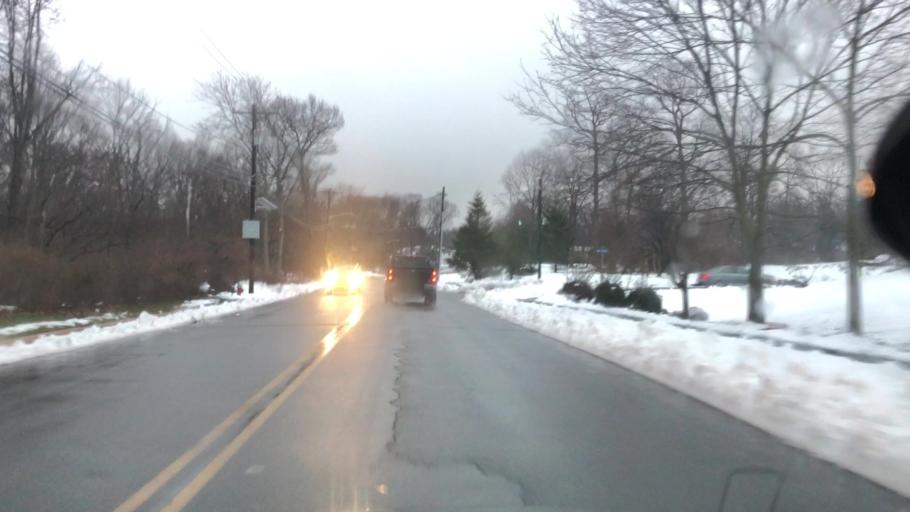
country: US
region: New Jersey
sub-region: Somerset County
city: Somerset
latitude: 40.5186
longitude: -74.5025
